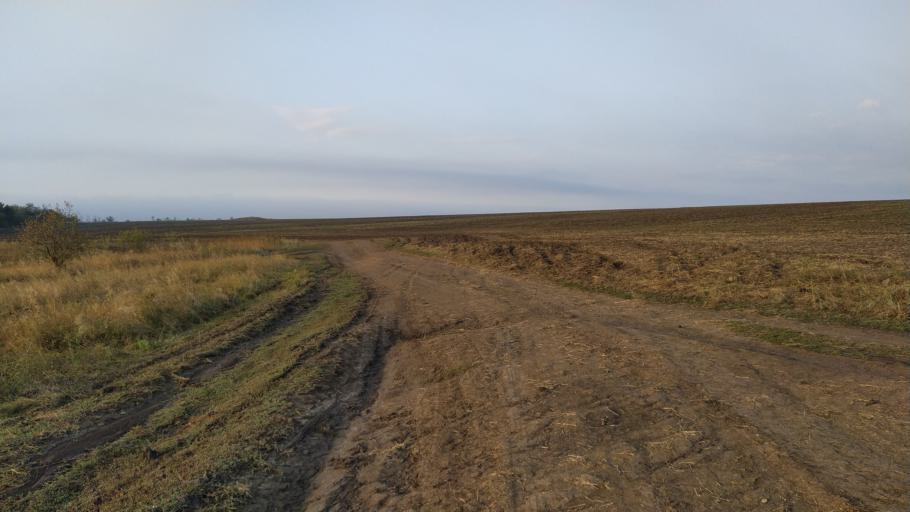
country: RU
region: Rostov
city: Gornyy
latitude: 47.8915
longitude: 40.2406
